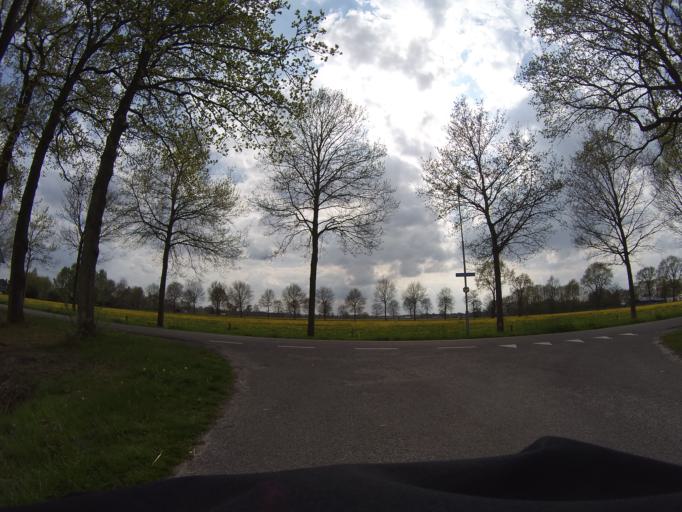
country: NL
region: Gelderland
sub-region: Gemeente Oldebroek
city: Oldebroek
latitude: 52.4612
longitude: 5.9523
